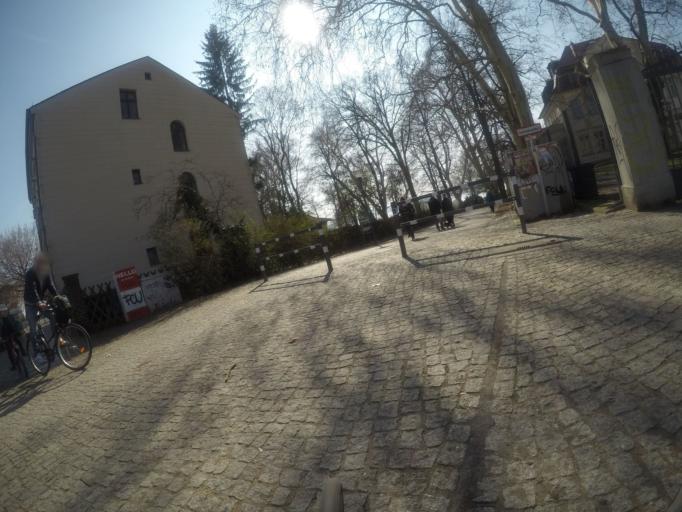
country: DE
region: Berlin
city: Friedrichshagen
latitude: 52.4457
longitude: 13.6267
